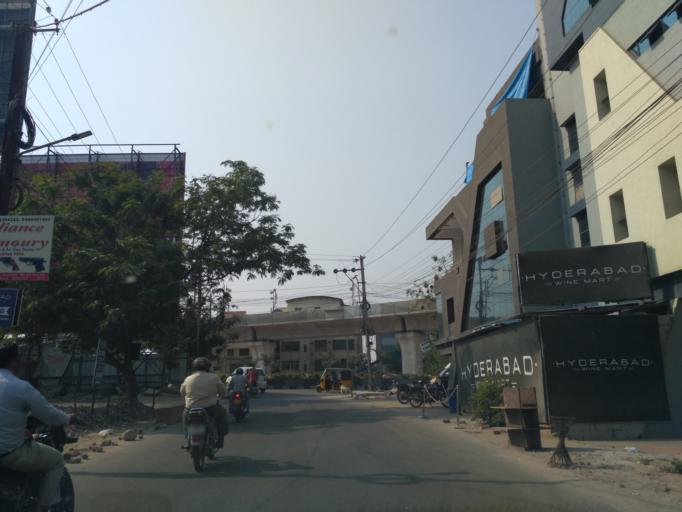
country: IN
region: Telangana
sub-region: Rangareddi
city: Kukatpalli
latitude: 17.4382
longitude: 78.3992
